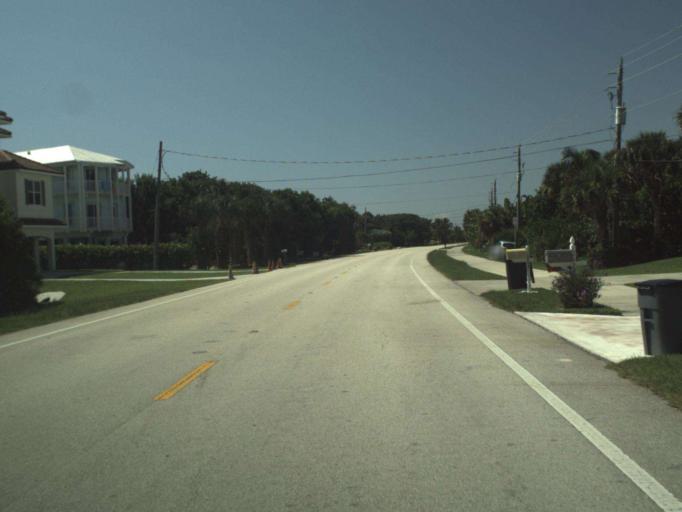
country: US
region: Florida
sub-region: Indian River County
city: Sebastian
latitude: 27.8241
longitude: -80.4294
